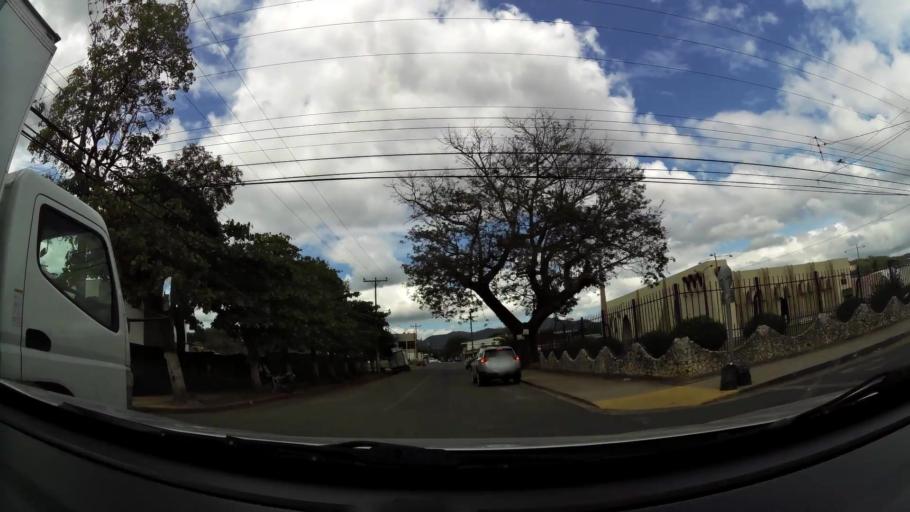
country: CR
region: Guanacaste
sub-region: Canton de Nicoya
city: Nicoya
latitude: 10.1439
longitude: -85.4544
